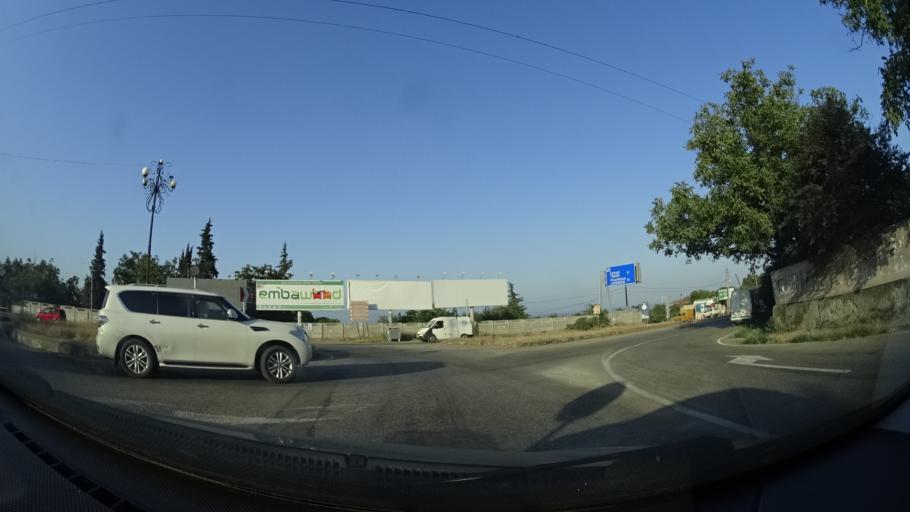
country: GE
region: Kakheti
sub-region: Gurjaani
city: Gurjaani
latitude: 41.6910
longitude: 45.8590
